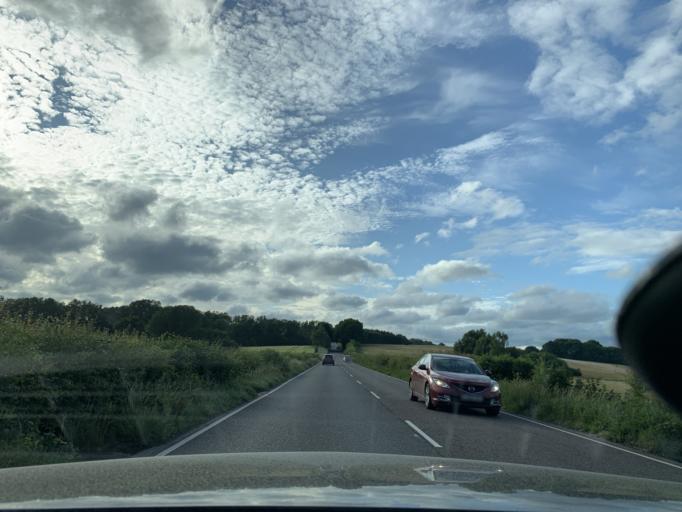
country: GB
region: England
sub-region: East Sussex
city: Battle
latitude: 50.9319
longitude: 0.5236
